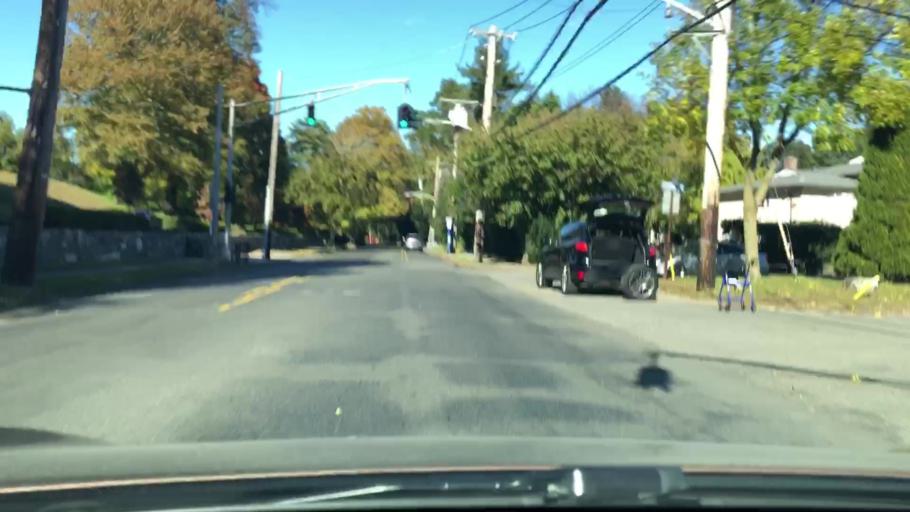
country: US
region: New York
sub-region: Westchester County
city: Bronxville
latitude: 40.9260
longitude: -73.8212
